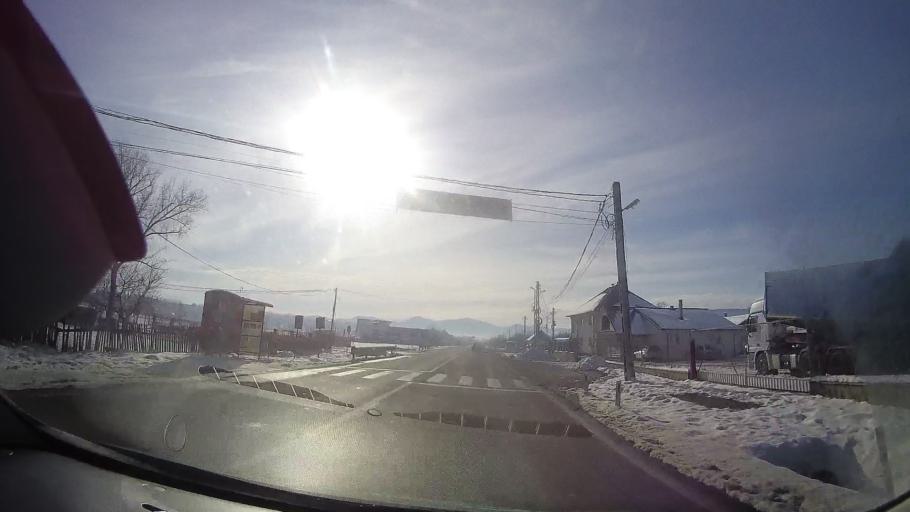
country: RO
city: Vanatori-Neamt
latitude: 47.1737
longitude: 26.3253
